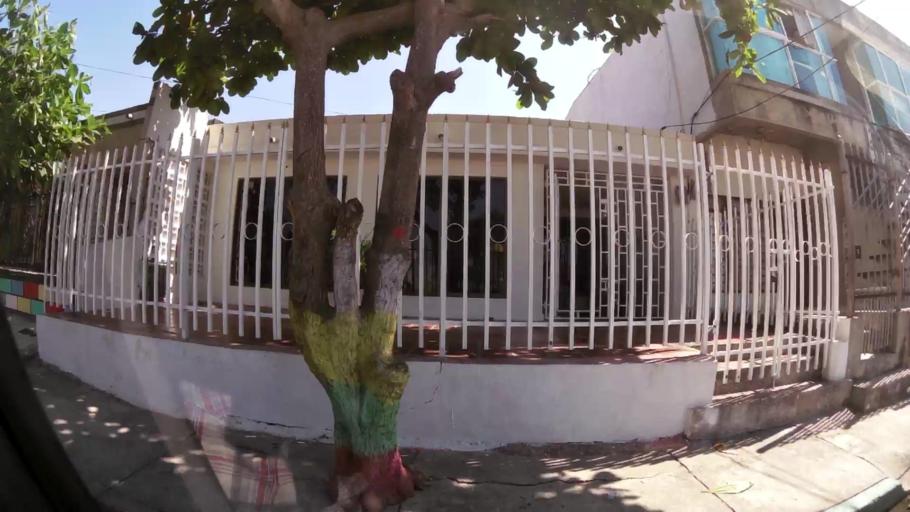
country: CO
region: Bolivar
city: Cartagena
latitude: 10.4361
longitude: -75.5265
